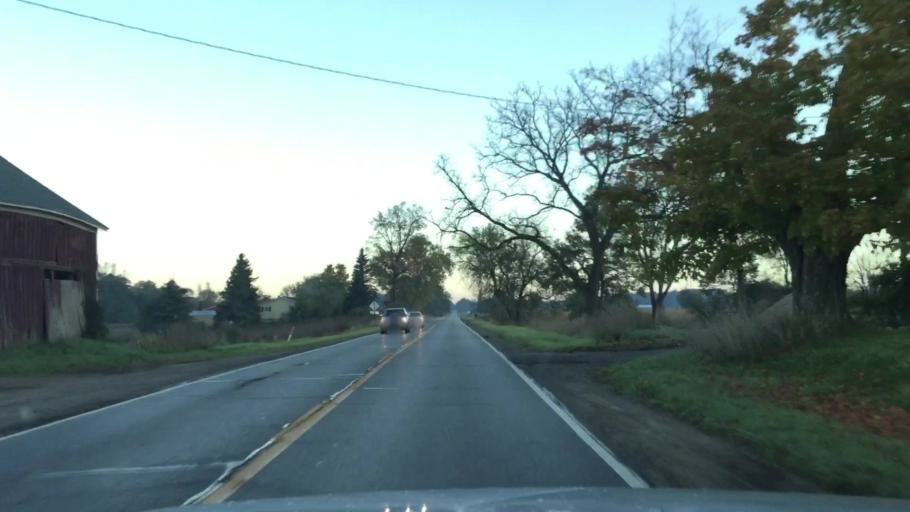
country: US
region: Michigan
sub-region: Livingston County
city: Howell
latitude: 42.6666
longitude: -83.9359
